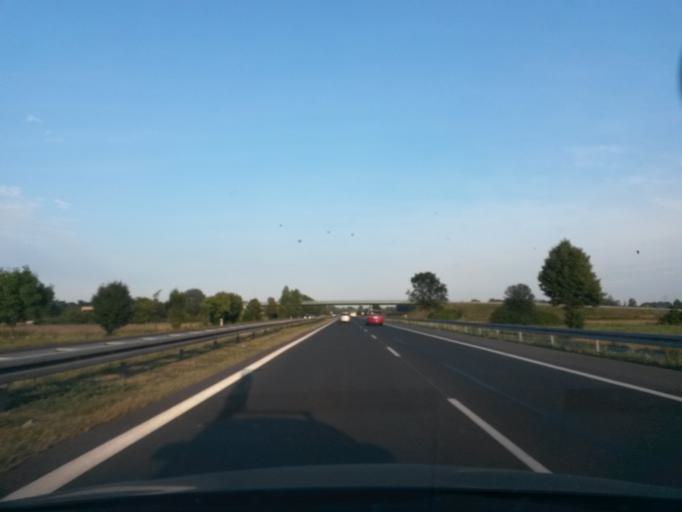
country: PL
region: Masovian Voivodeship
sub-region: Powiat nowodworski
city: Nowy Dwor Mazowiecki
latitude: 52.4174
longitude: 20.6757
